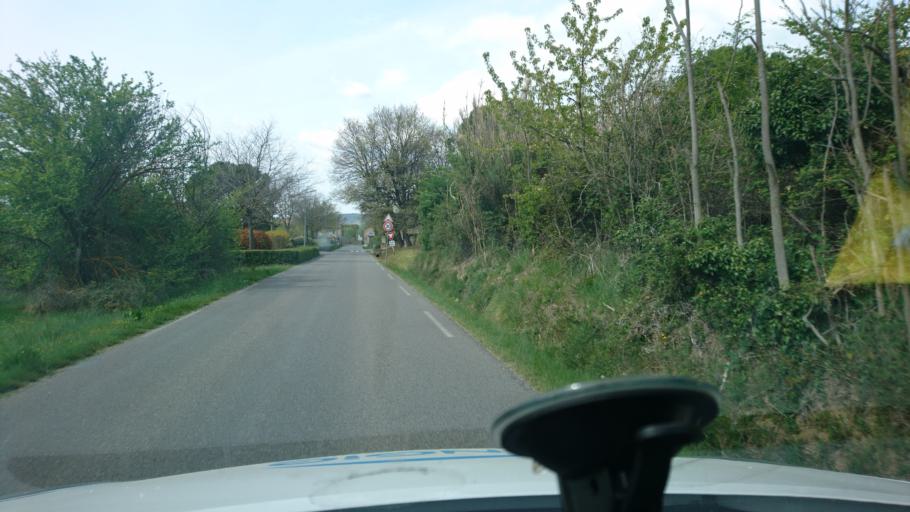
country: FR
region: Provence-Alpes-Cote d'Azur
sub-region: Departement du Vaucluse
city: Oppede
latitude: 43.8506
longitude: 5.1626
